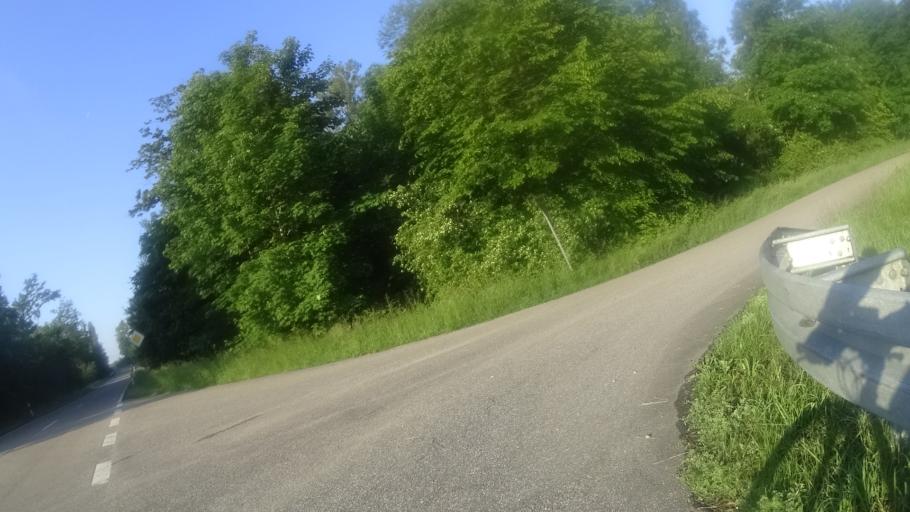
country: FR
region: Alsace
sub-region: Departement du Bas-Rhin
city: Drusenheim
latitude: 48.7451
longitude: 7.9735
